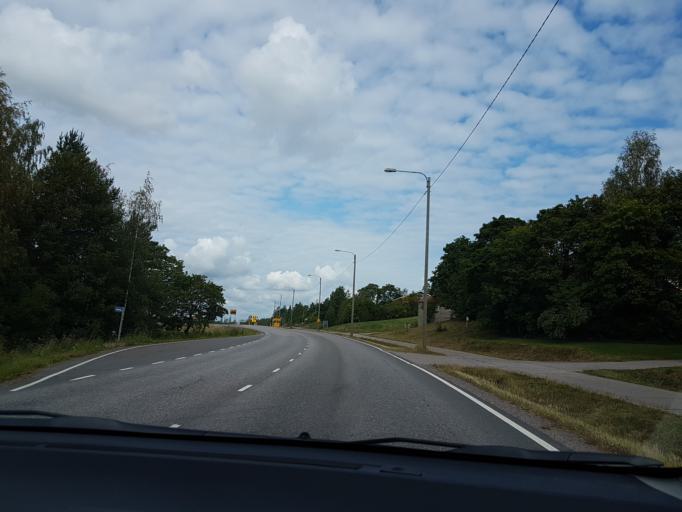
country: FI
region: Uusimaa
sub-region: Helsinki
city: Pornainen
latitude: 60.4856
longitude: 25.3674
